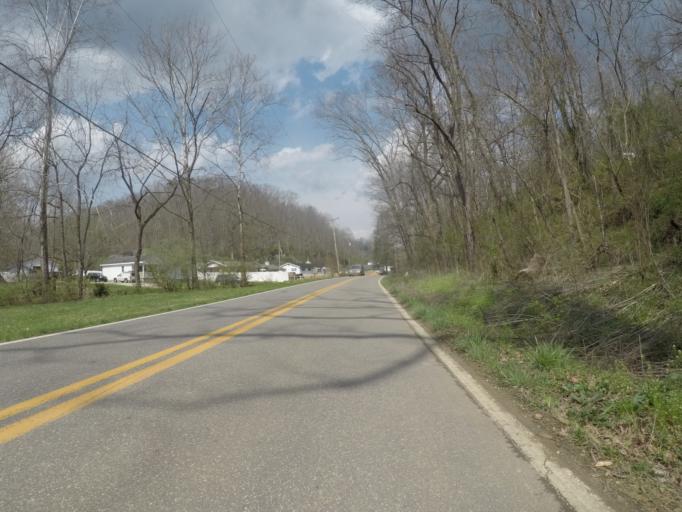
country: US
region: West Virginia
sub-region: Cabell County
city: Pea Ridge
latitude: 38.3374
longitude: -82.3398
